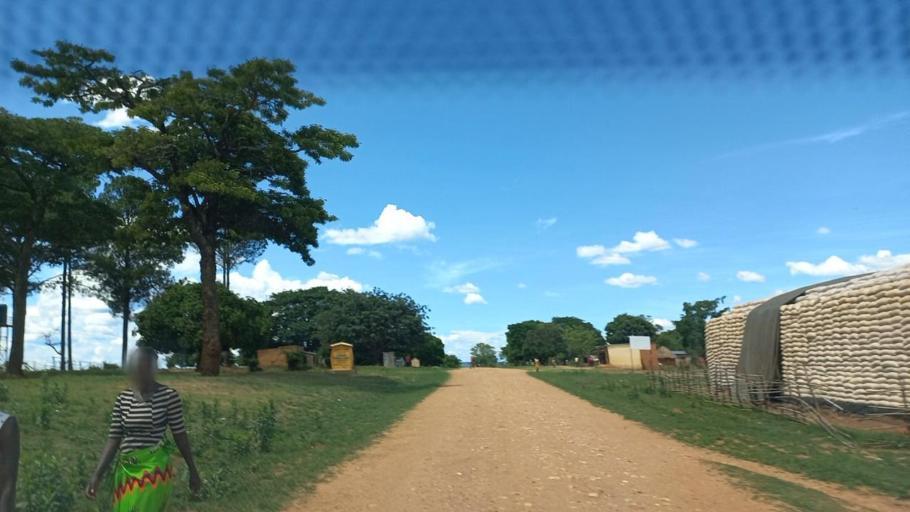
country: ZM
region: North-Western
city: Mwinilunga
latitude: -12.3054
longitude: 24.2621
